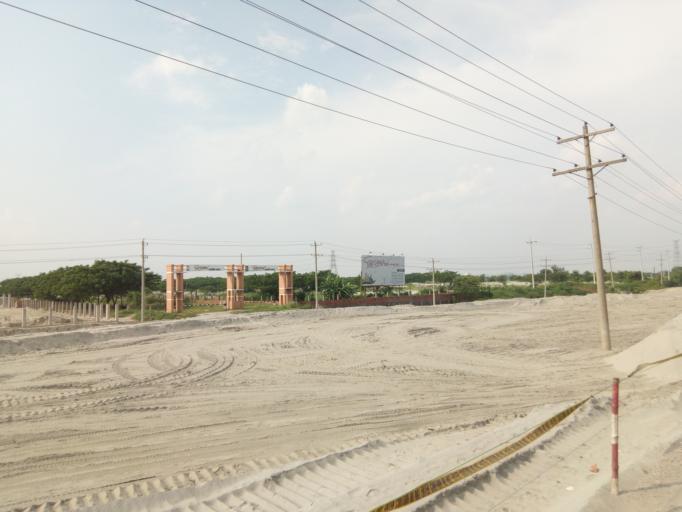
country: BD
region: Dhaka
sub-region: Dhaka
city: Dhaka
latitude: 23.6662
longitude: 90.3942
